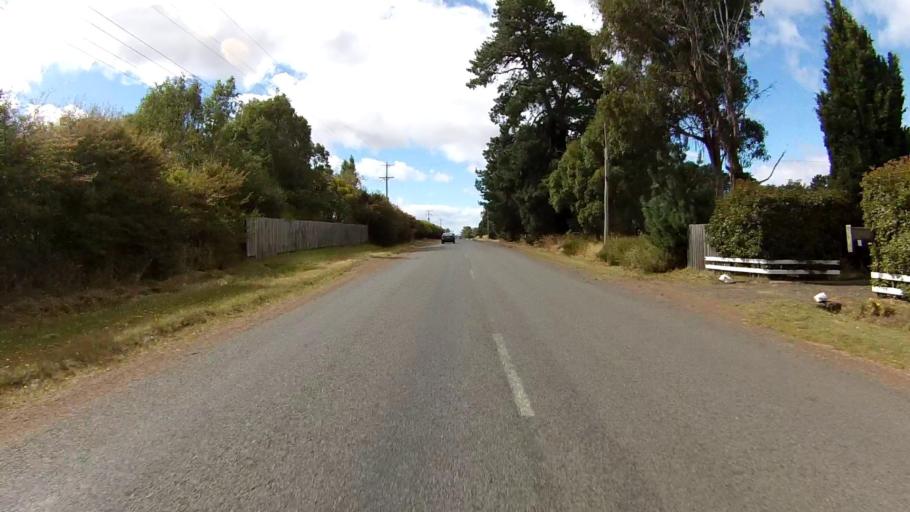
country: AU
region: Tasmania
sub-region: Northern Midlands
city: Evandale
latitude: -41.6067
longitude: 147.2831
